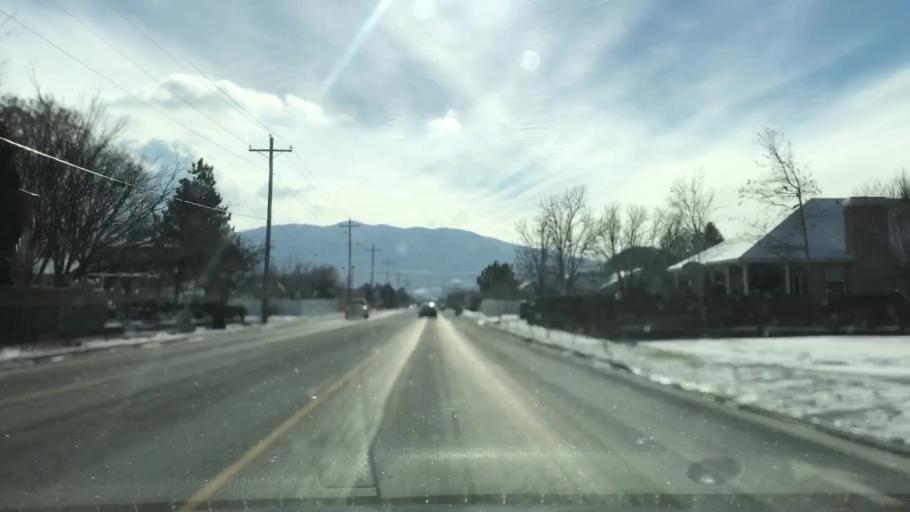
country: US
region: Utah
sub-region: Salt Lake County
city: Draper
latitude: 40.5231
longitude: -111.8818
